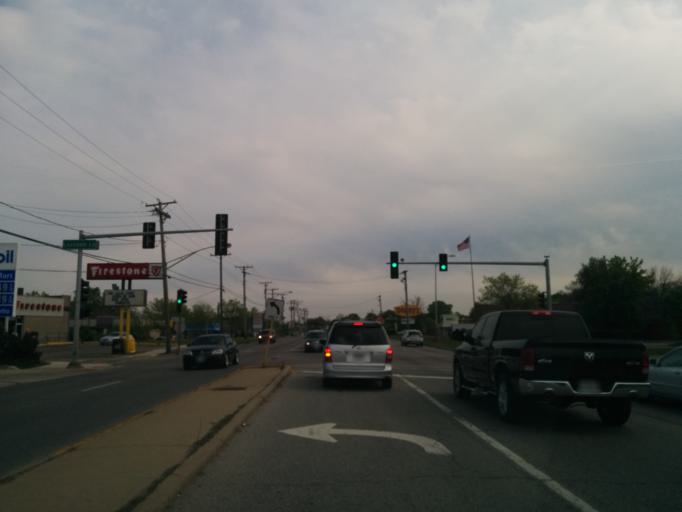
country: US
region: Illinois
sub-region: Kane County
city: North Aurora
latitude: 41.7920
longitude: -88.3227
